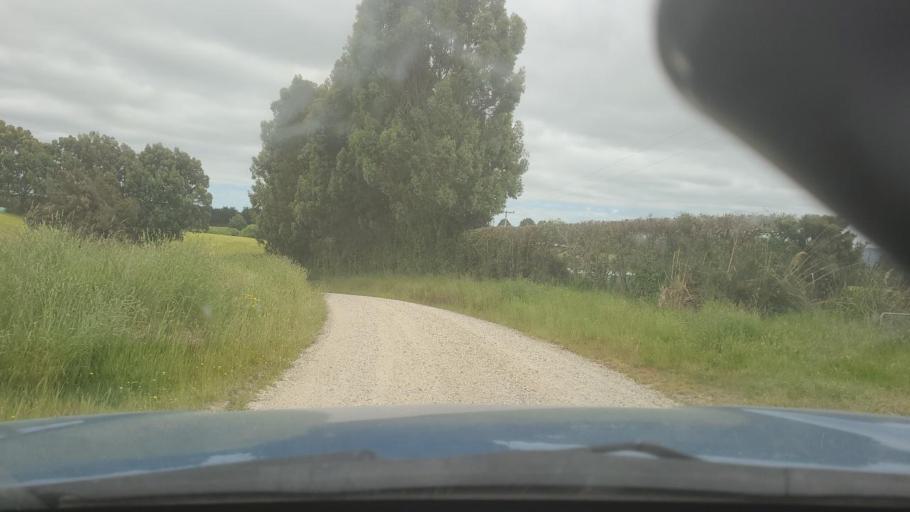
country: NZ
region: Southland
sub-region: Gore District
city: Gore
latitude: -46.2149
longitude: 168.7263
